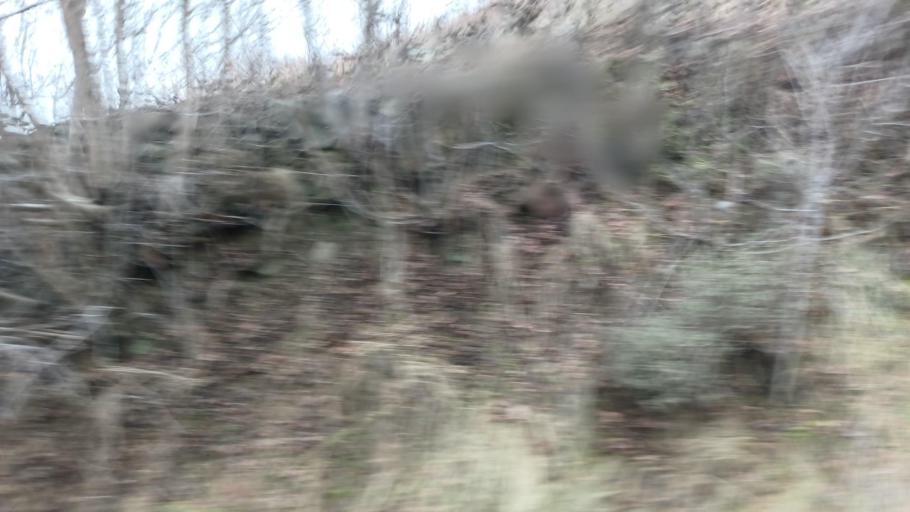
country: CY
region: Limassol
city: Kyperounta
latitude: 34.9256
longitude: 32.9711
